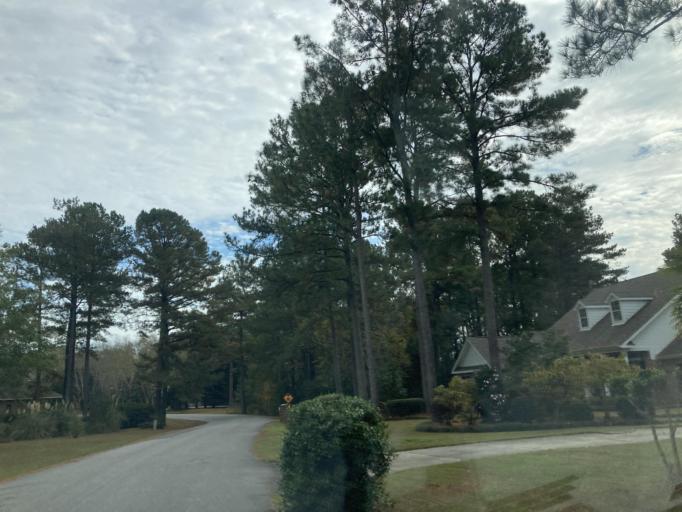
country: US
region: Mississippi
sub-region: Lamar County
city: West Hattiesburg
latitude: 31.3306
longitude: -89.4131
